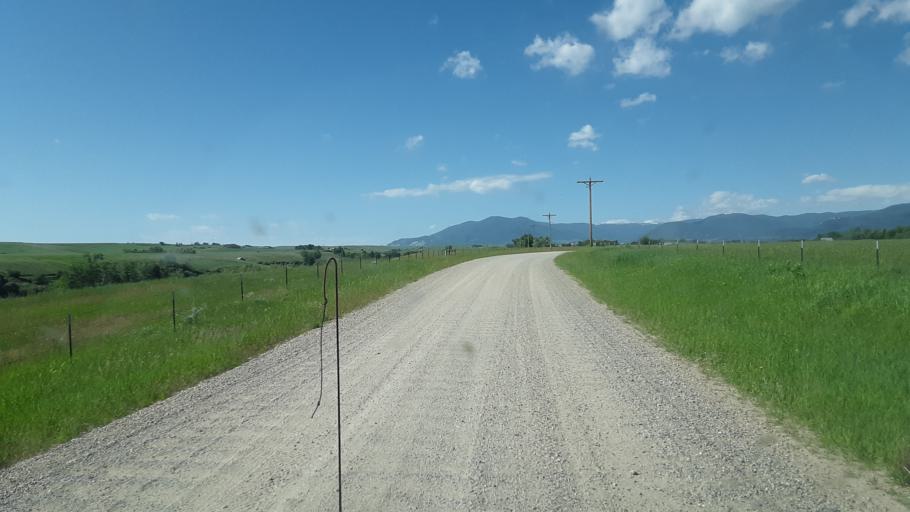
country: US
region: Montana
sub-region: Carbon County
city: Red Lodge
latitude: 45.2826
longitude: -109.1904
